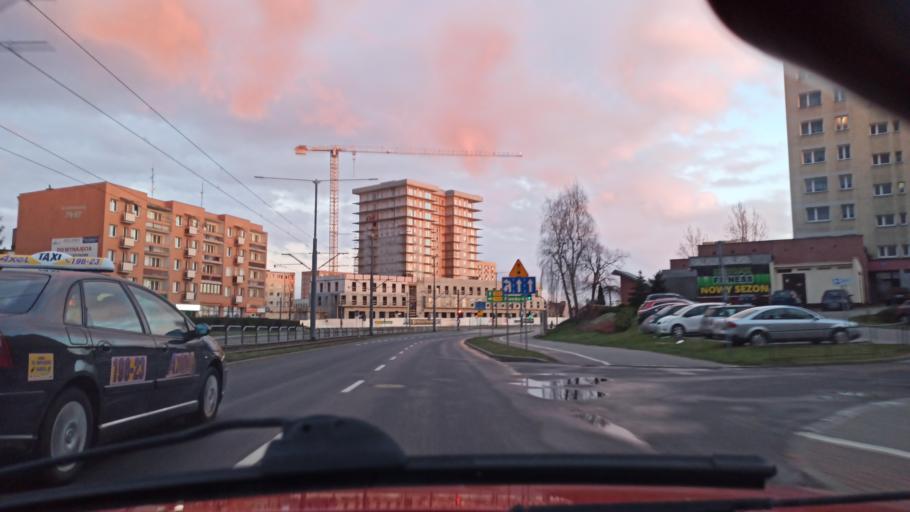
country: PL
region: Warmian-Masurian Voivodeship
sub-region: Powiat elblaski
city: Elblag
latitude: 54.1683
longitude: 19.4061
